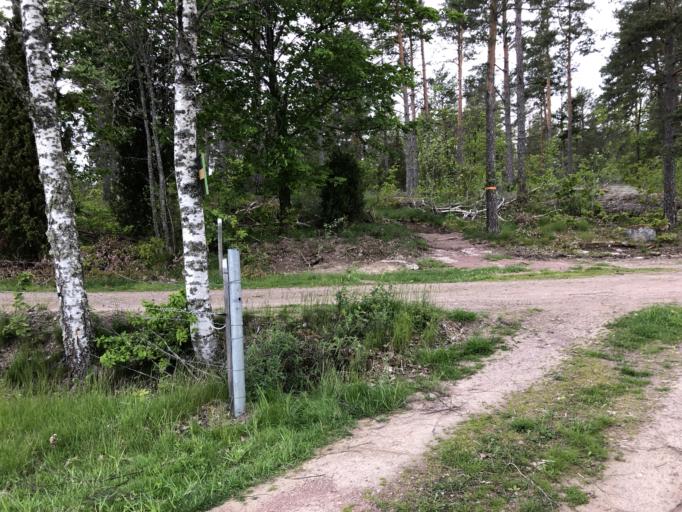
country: SE
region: Kalmar
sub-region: Oskarshamns Kommun
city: Oskarshamn
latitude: 57.4218
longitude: 16.2353
